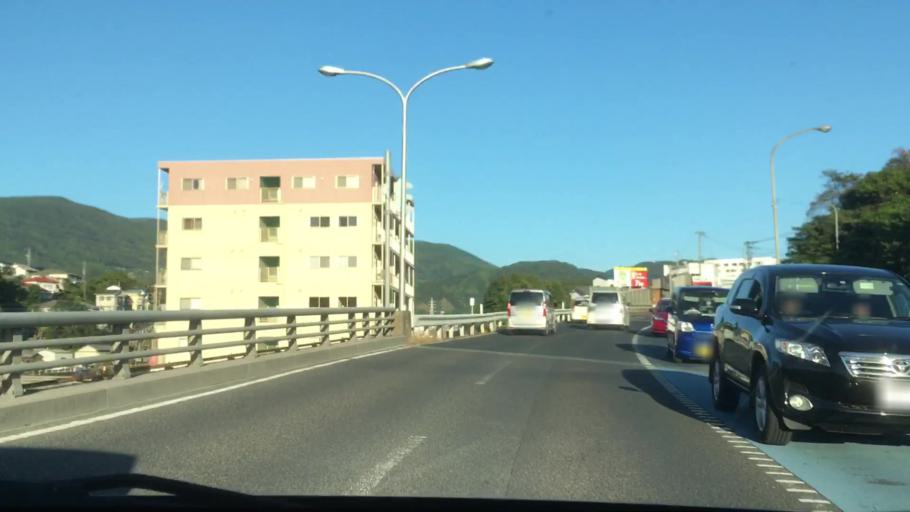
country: JP
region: Nagasaki
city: Sasebo
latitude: 33.1588
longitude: 129.7599
